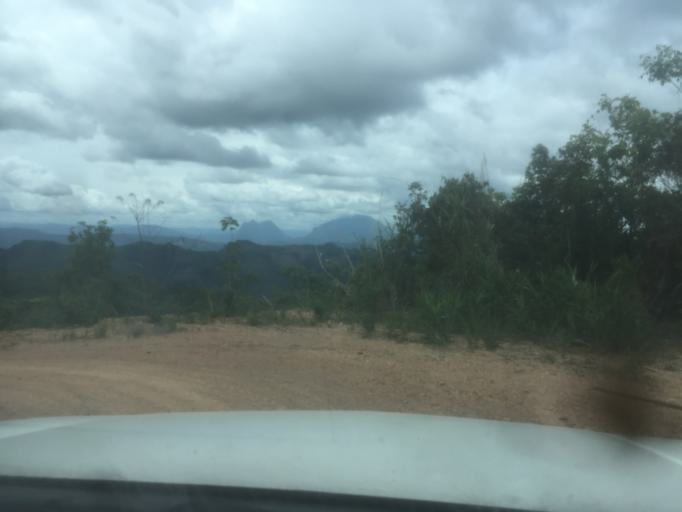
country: LA
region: Phongsali
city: Khoa
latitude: 20.9275
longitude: 102.5320
